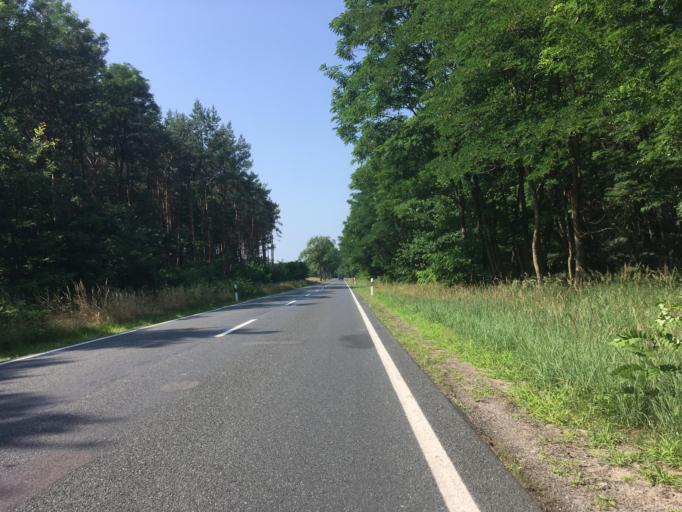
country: DE
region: Brandenburg
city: Golzow
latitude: 52.2944
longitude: 12.6741
